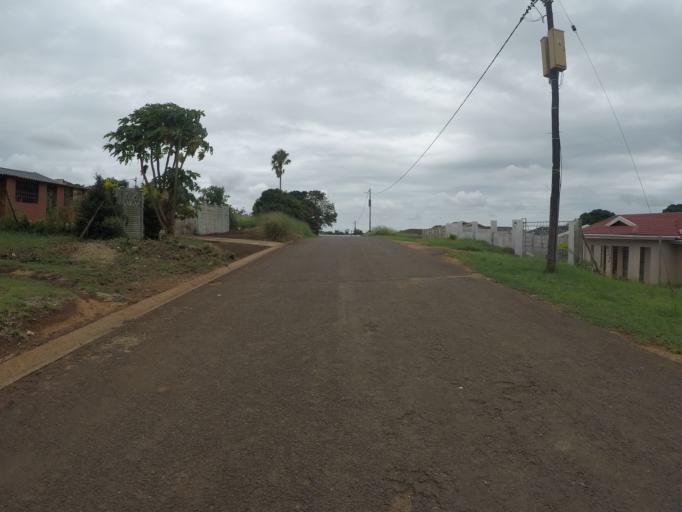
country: ZA
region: KwaZulu-Natal
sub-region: uThungulu District Municipality
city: Empangeni
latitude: -28.7769
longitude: 31.8609
